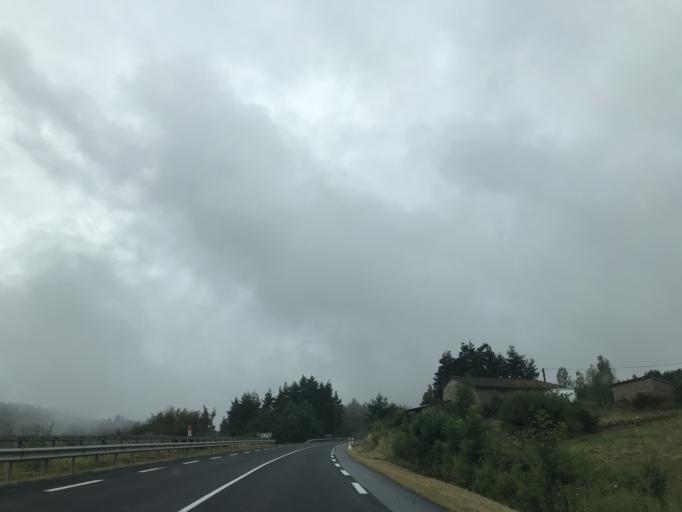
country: FR
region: Auvergne
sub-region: Departement du Puy-de-Dome
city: Arlanc
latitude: 45.3628
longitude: 3.7528
